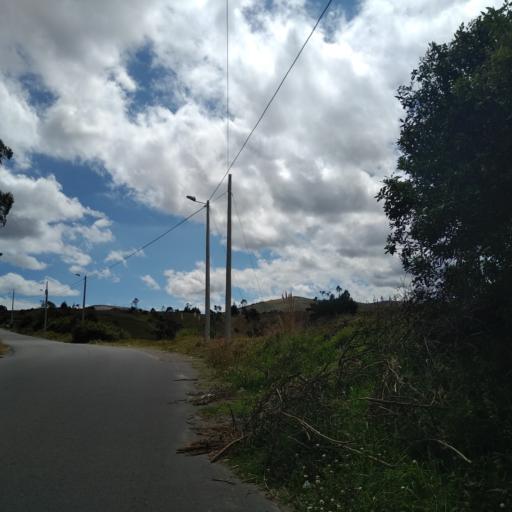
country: EC
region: Cotopaxi
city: Saquisili
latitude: -0.7525
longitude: -78.7268
